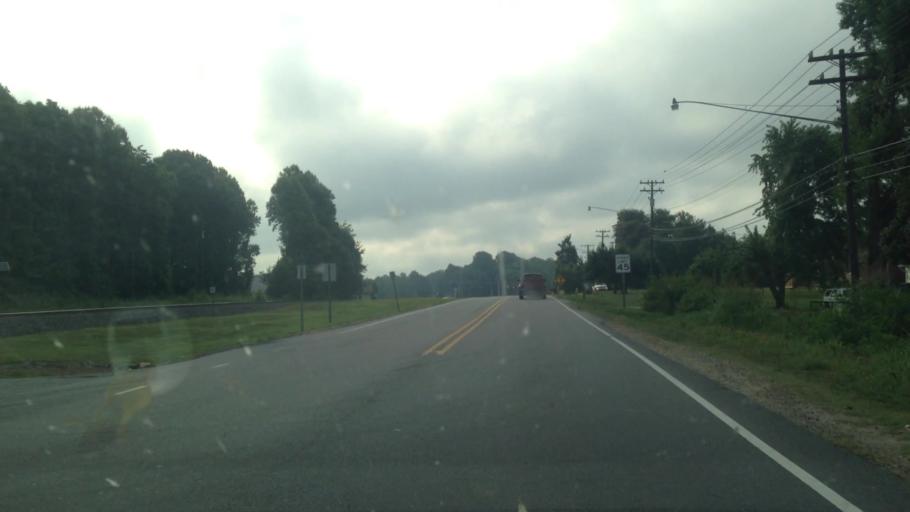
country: US
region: North Carolina
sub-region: Forsyth County
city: Kernersville
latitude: 36.1360
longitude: -80.1004
